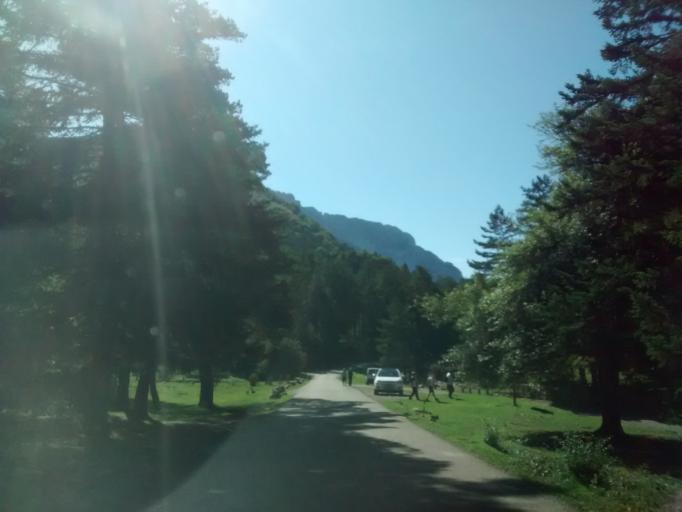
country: ES
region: Aragon
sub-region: Provincia de Huesca
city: Aragues del Puerto
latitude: 42.8334
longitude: -0.7111
